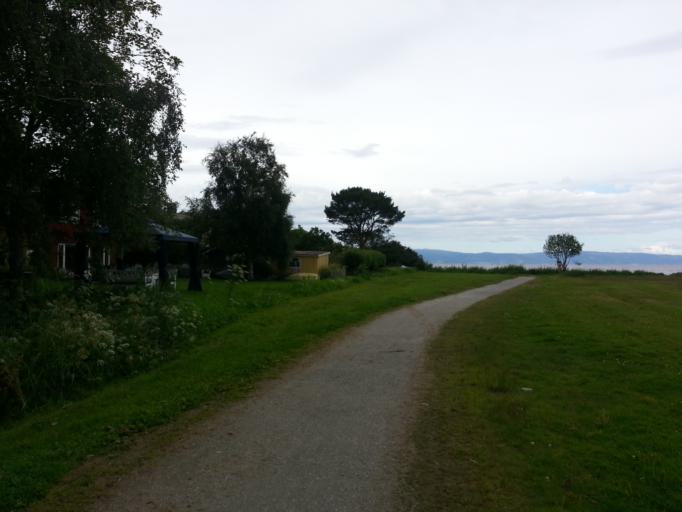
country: NO
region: Sor-Trondelag
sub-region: Trondheim
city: Trondheim
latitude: 63.4313
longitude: 10.5203
